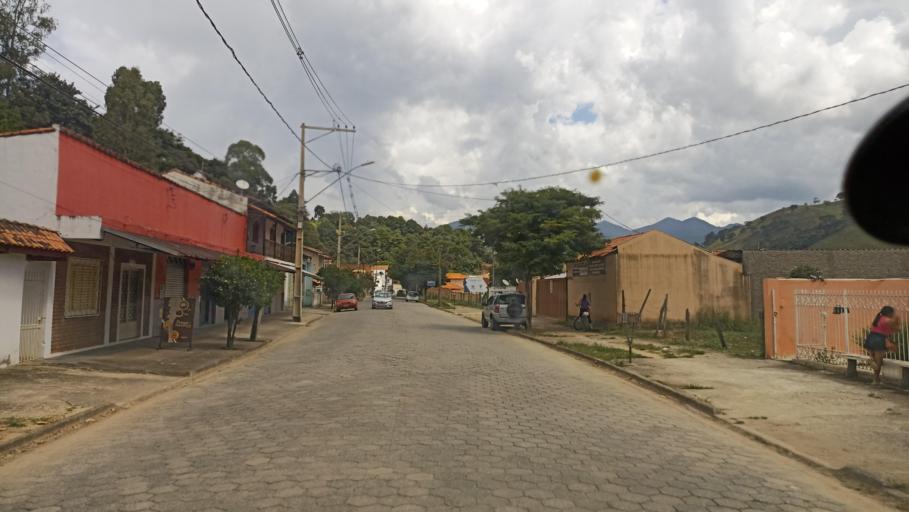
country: BR
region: Minas Gerais
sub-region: Passa Quatro
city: Passa Quatro
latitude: -22.3764
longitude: -44.9636
